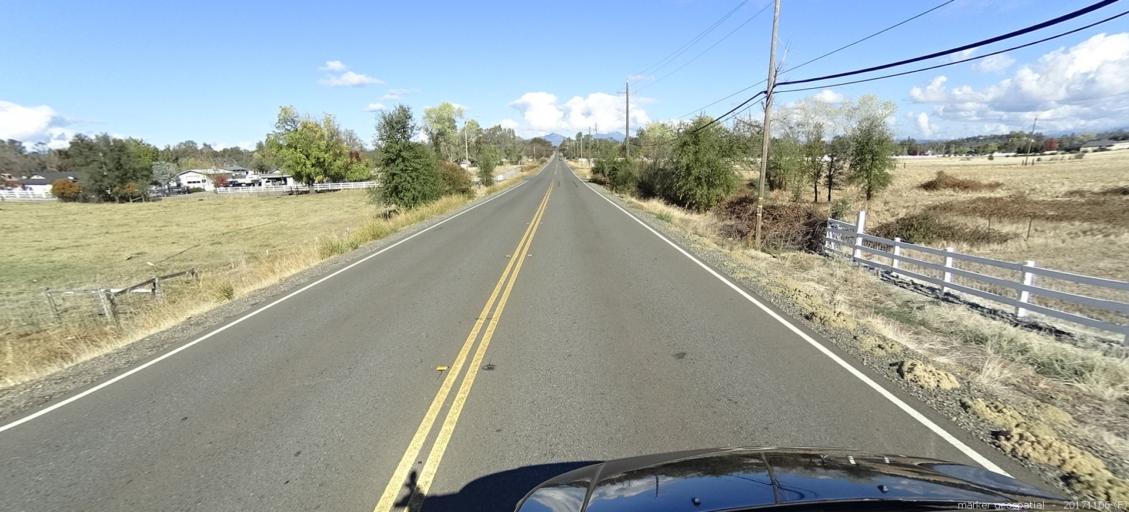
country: US
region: California
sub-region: Shasta County
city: Palo Cedro
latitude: 40.5790
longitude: -122.2388
